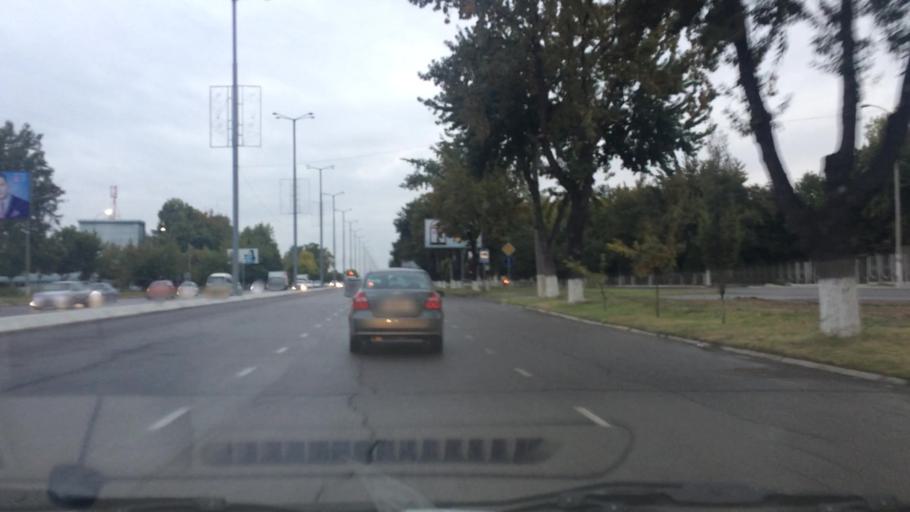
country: UZ
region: Toshkent Shahri
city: Tashkent
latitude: 41.2542
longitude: 69.1892
